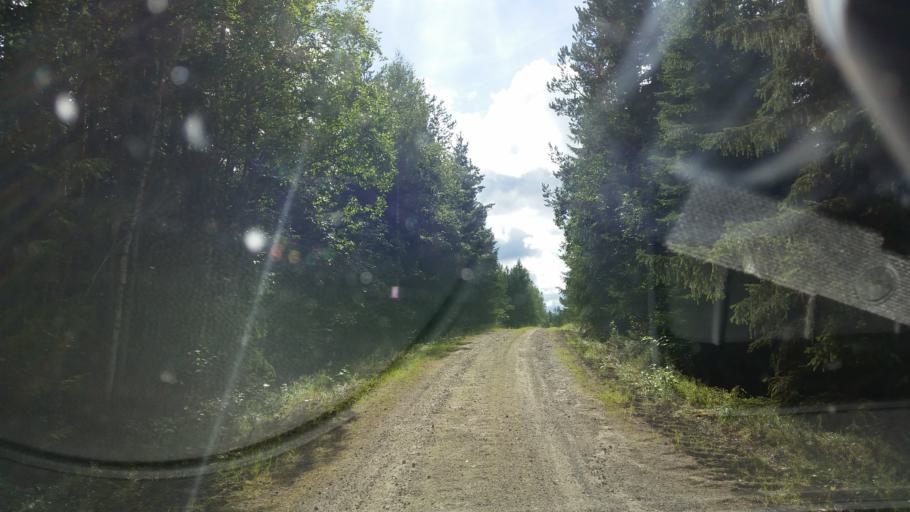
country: SE
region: Vaesternorrland
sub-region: Ange Kommun
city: Ange
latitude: 62.2325
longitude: 15.7087
